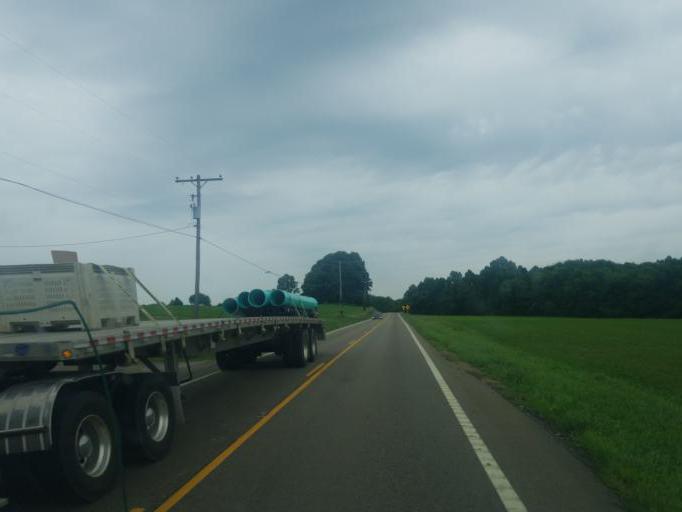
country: US
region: Ohio
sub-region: Stark County
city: Minerva
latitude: 40.6927
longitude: -81.0142
